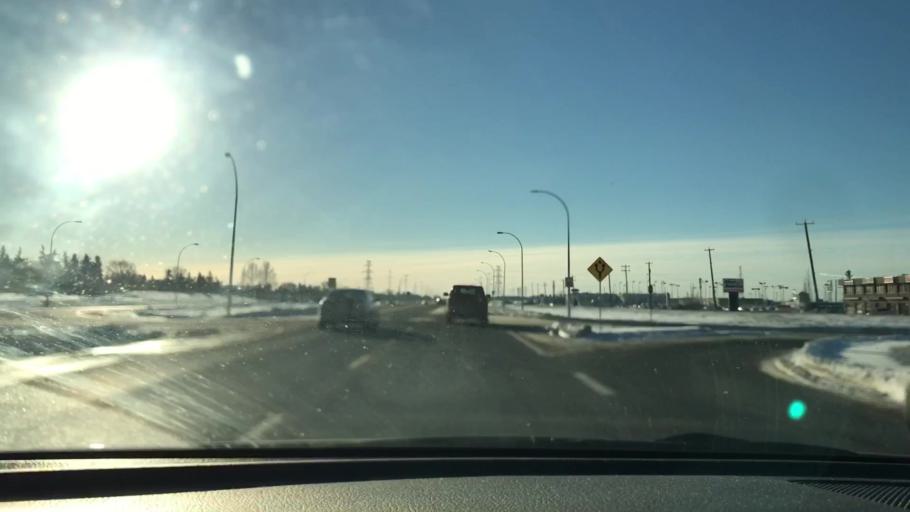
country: CA
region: Alberta
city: Edmonton
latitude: 53.4690
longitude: -113.4669
